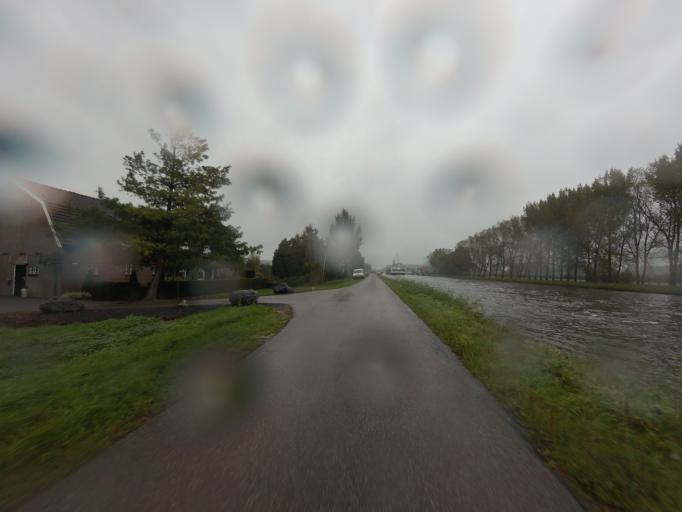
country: NL
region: Utrecht
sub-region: Gemeente Vianen
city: Vianen
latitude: 51.9462
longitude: 5.0483
